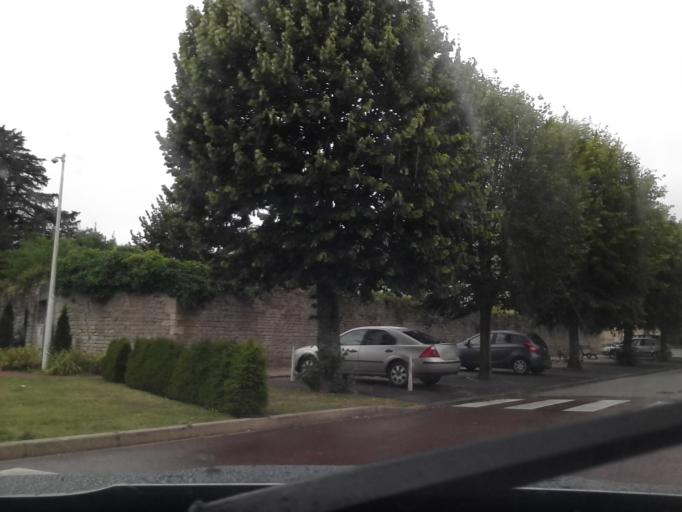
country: FR
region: Lower Normandy
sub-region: Departement de la Manche
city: Carentan
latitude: 49.3050
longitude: -1.2417
